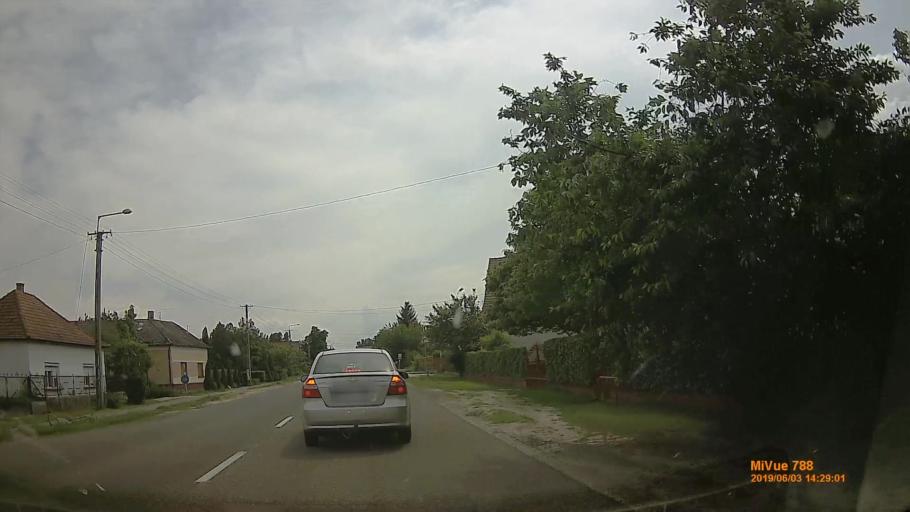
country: HU
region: Bacs-Kiskun
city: Tiszakecske
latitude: 46.9741
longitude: 20.1115
